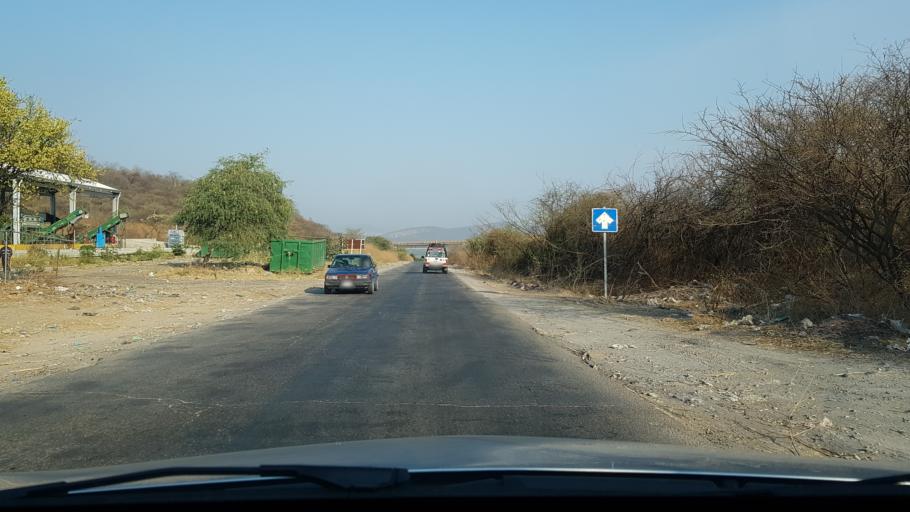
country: MX
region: Morelos
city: Tlaltizapan
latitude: 18.6771
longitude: -99.0784
